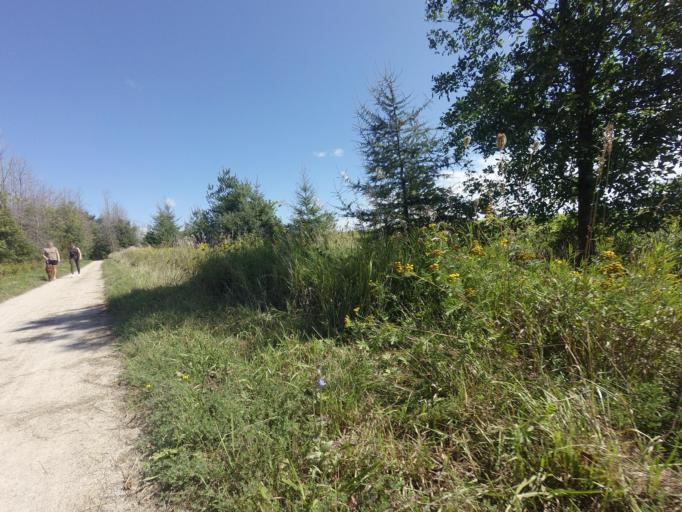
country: CA
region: Ontario
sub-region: Wellington County
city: Guelph
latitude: 43.7326
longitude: -80.3682
